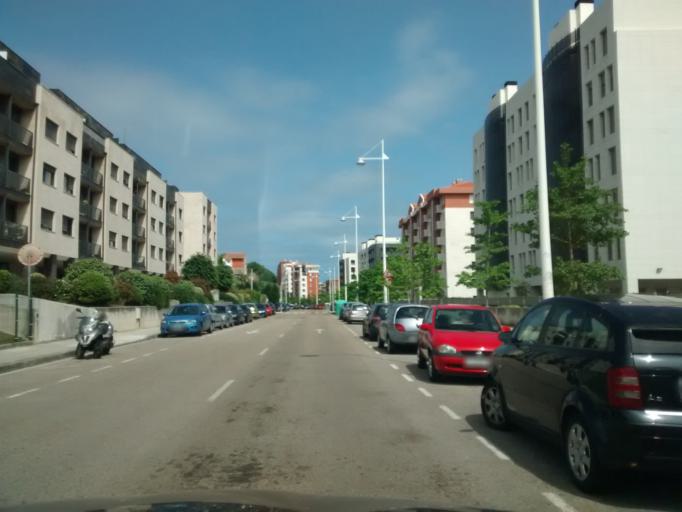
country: ES
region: Cantabria
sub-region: Provincia de Cantabria
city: Santander
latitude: 43.4731
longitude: -3.8134
